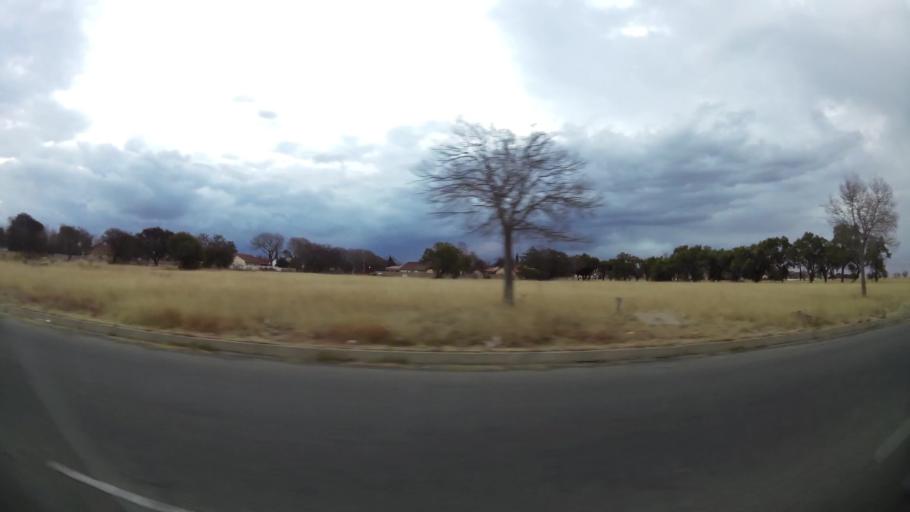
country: ZA
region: Orange Free State
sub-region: Lejweleputswa District Municipality
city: Welkom
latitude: -27.9612
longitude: 26.7520
